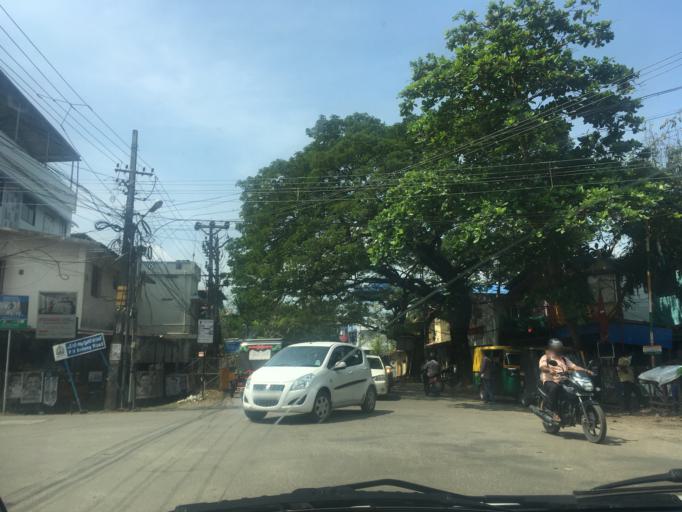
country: IN
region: Kerala
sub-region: Ernakulam
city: Cochin
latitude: 9.9775
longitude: 76.2944
